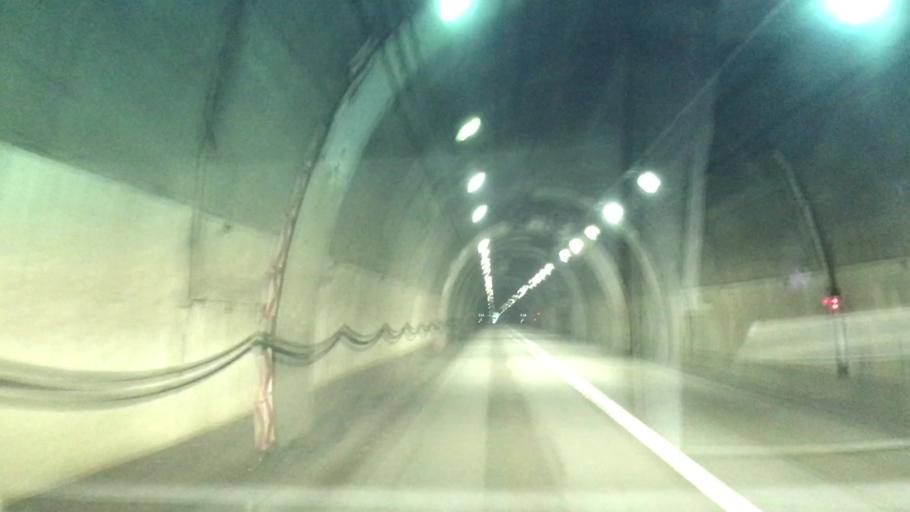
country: JP
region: Hokkaido
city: Yoichi
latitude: 43.0507
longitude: 140.6818
